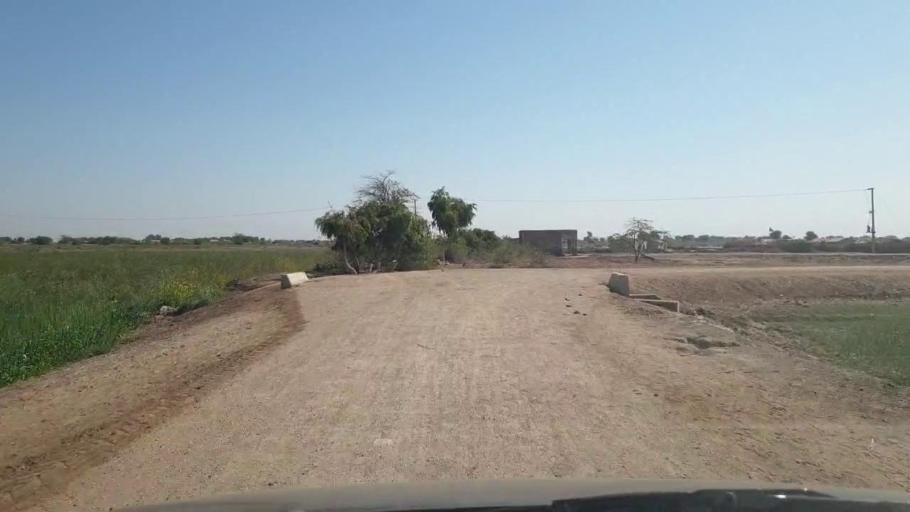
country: PK
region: Sindh
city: Umarkot
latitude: 25.4169
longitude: 69.6600
